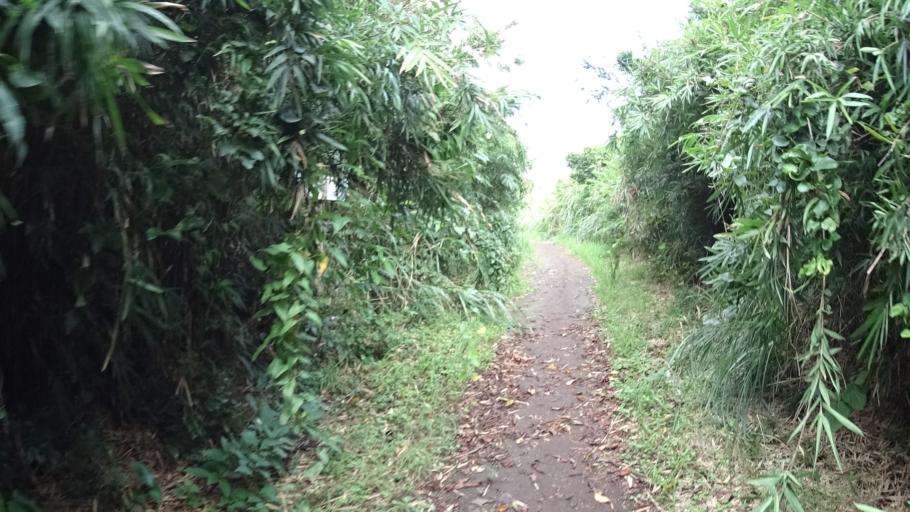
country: JP
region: Kanagawa
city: Miura
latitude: 35.1334
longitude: 139.6165
